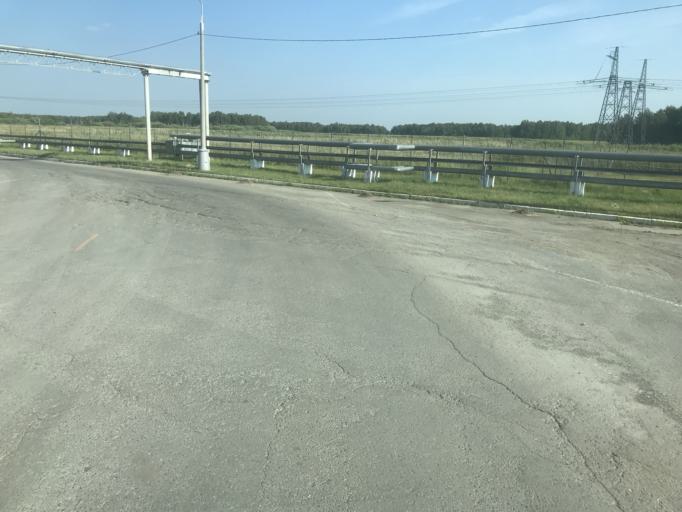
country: RU
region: Kurgan
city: Petukhovo
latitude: 55.0906
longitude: 68.2410
